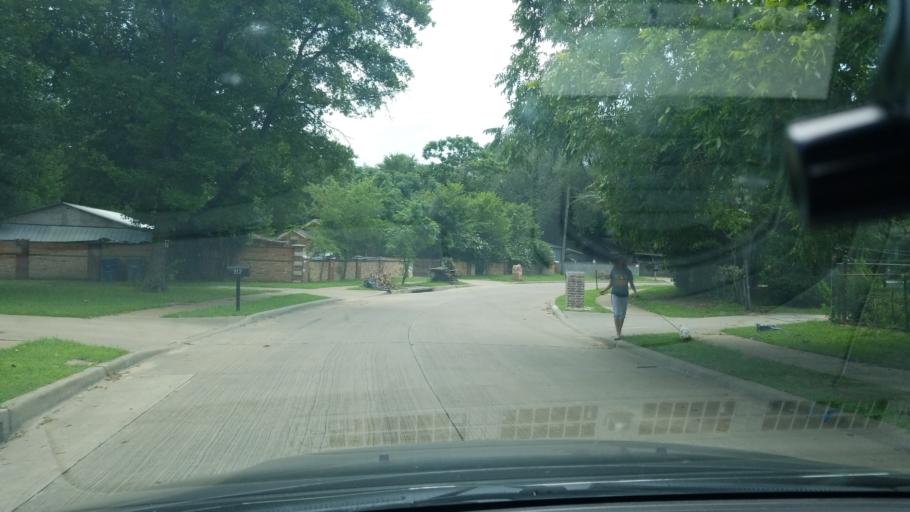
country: US
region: Texas
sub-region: Dallas County
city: Balch Springs
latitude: 32.7171
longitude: -96.6583
